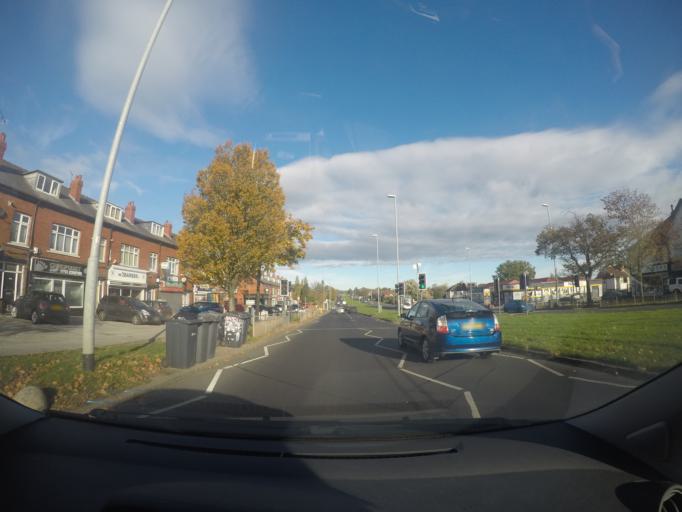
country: GB
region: England
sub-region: City and Borough of Leeds
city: Chapel Allerton
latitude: 53.8189
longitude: -1.5032
